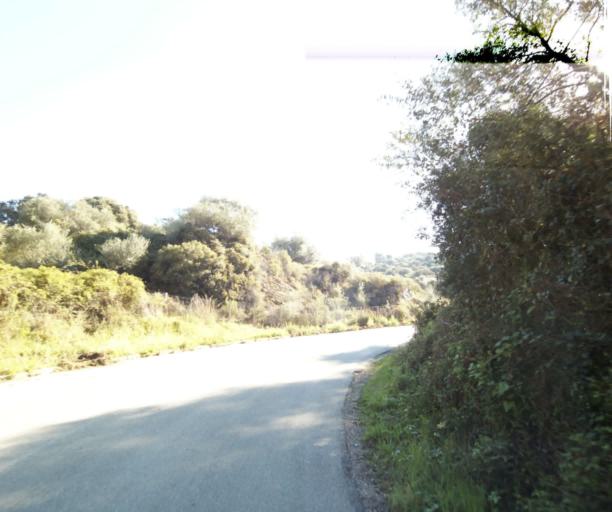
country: FR
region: Corsica
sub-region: Departement de la Corse-du-Sud
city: Propriano
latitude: 41.6664
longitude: 8.8937
